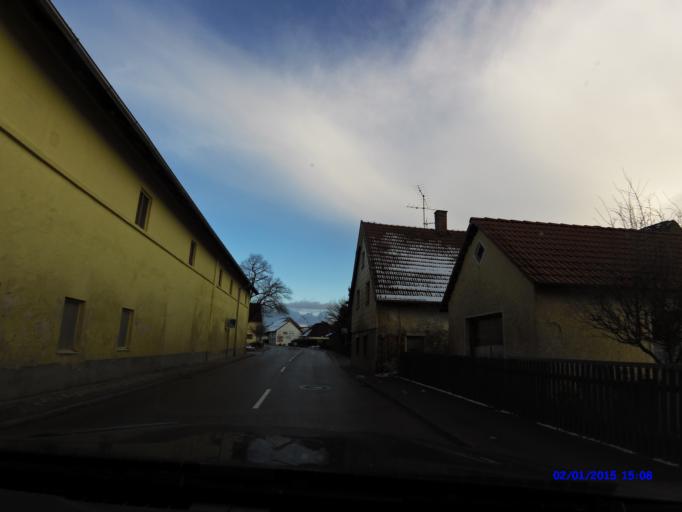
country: DE
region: Bavaria
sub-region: Upper Bavaria
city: Rudelzhausen
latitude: 48.6292
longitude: 11.7436
